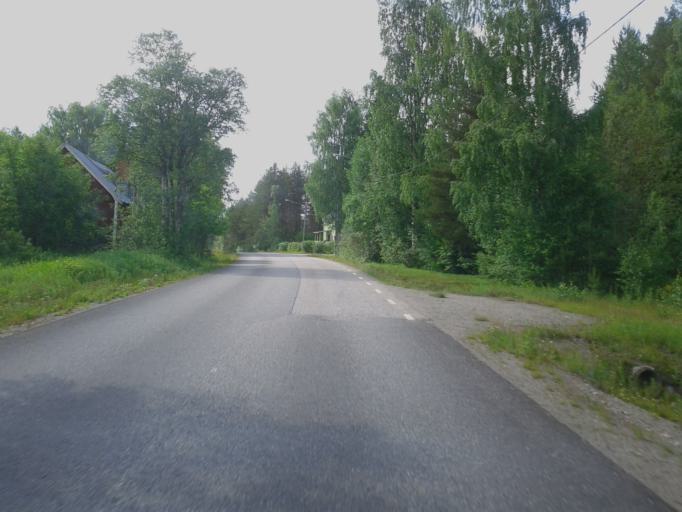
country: SE
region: Vaesterbotten
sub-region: Sorsele Kommun
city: Sorsele
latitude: 65.2797
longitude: 17.9315
